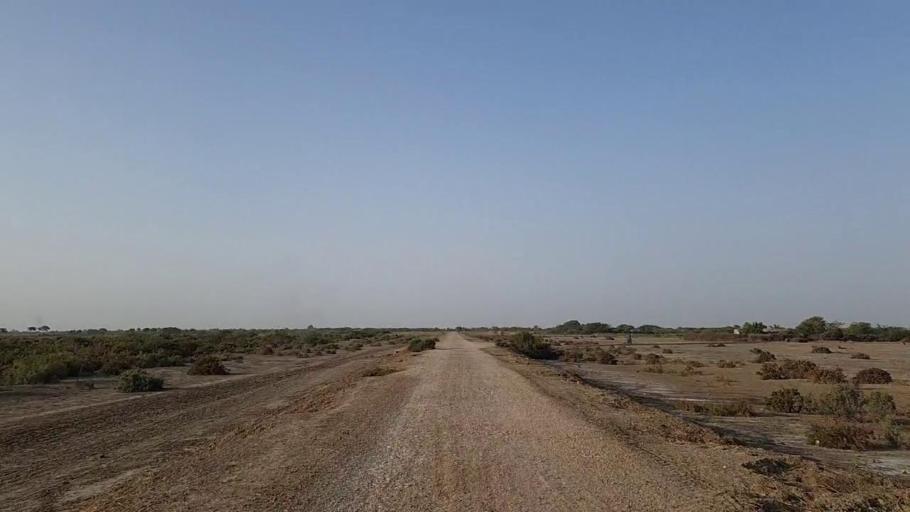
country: PK
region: Sindh
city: Jati
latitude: 24.3755
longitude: 68.1478
